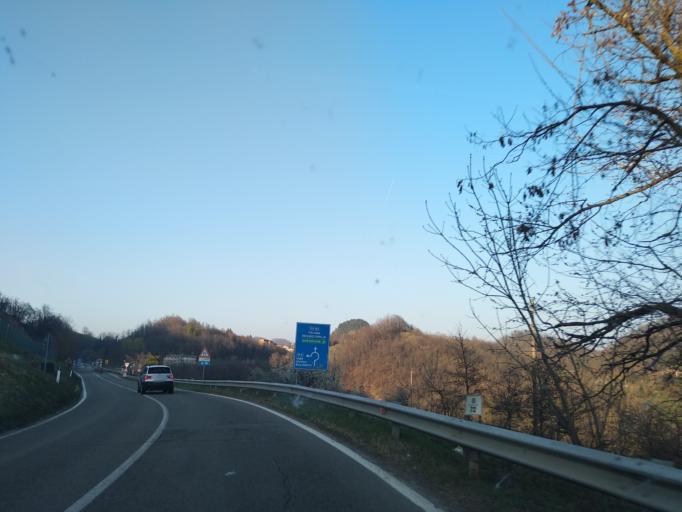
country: IT
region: Emilia-Romagna
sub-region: Provincia di Reggio Emilia
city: Felina
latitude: 44.4450
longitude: 10.4466
